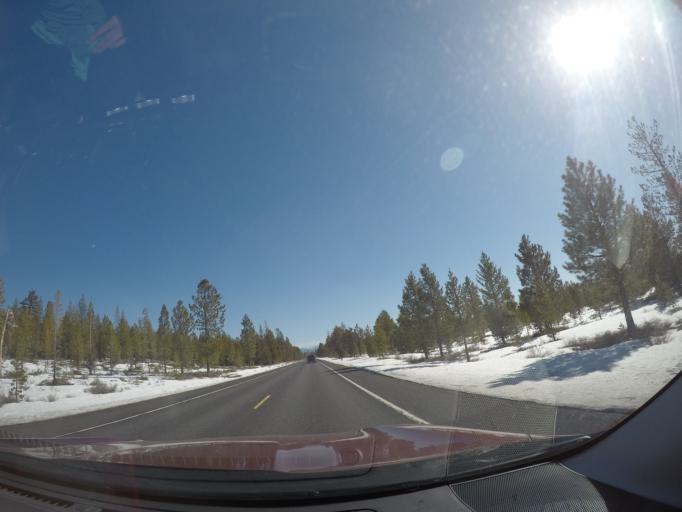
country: US
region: Oregon
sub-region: Deschutes County
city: Three Rivers
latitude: 43.8601
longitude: -121.5279
